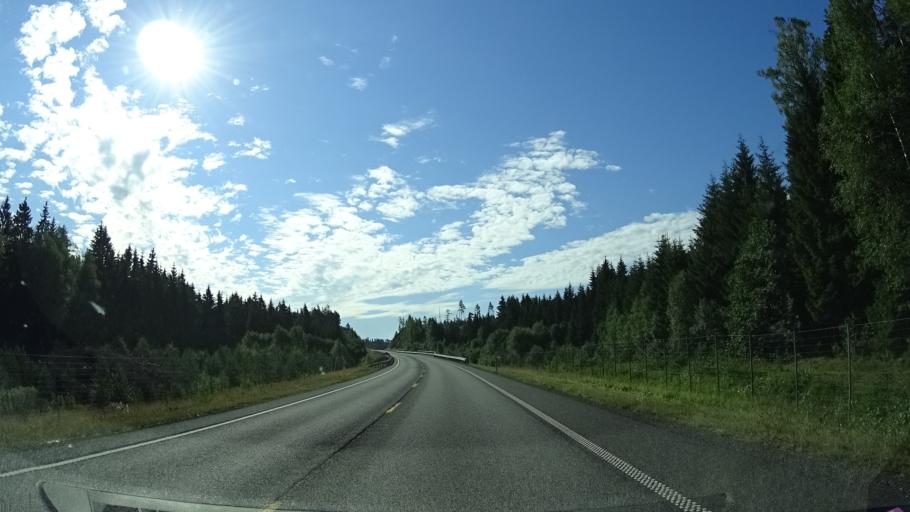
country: NO
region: Ostfold
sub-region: Marker
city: Orje
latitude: 59.5247
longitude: 11.5782
